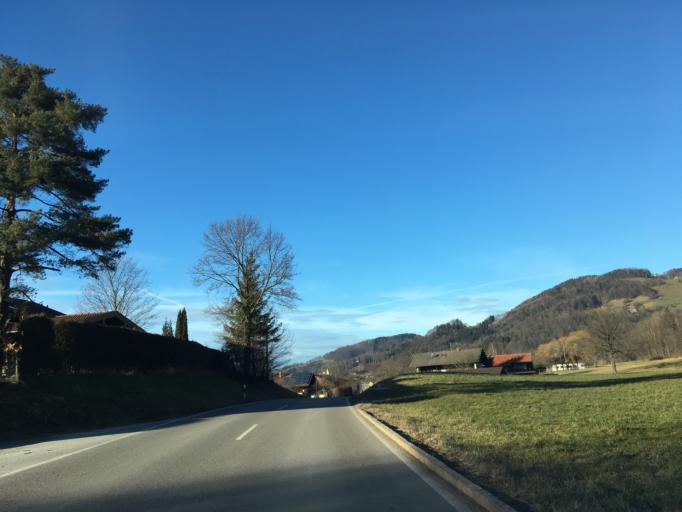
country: DE
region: Bavaria
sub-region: Upper Bavaria
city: Nussdorf am Inn
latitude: 47.7290
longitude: 12.1618
